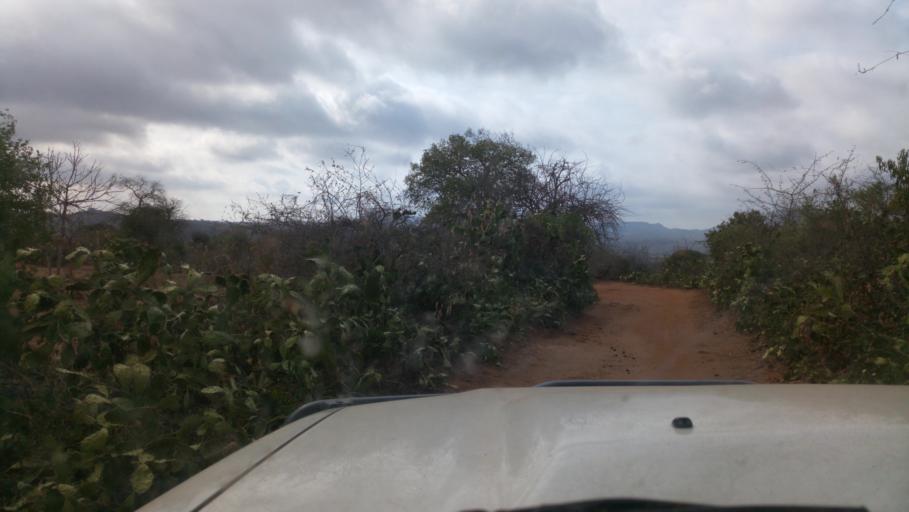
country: KE
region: Kitui
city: Kitui
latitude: -1.8571
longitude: 38.2569
